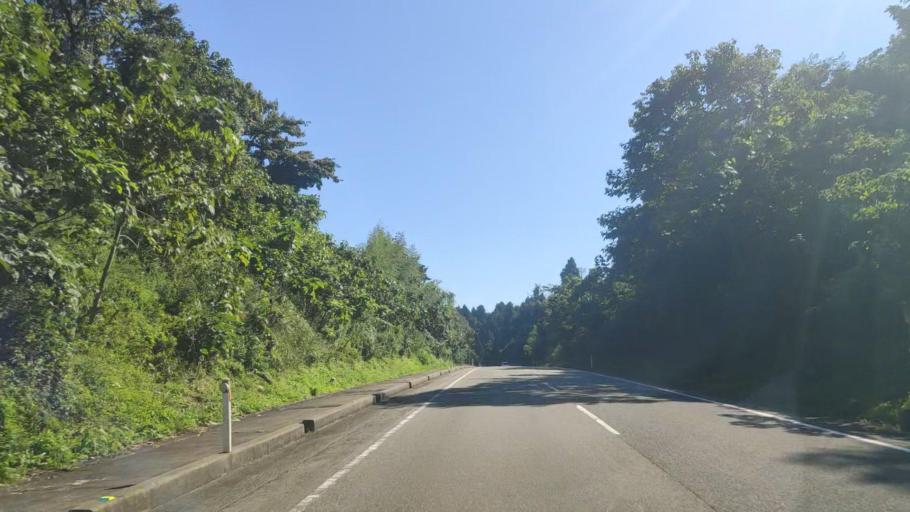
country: JP
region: Ishikawa
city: Nanao
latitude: 37.3797
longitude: 137.2337
